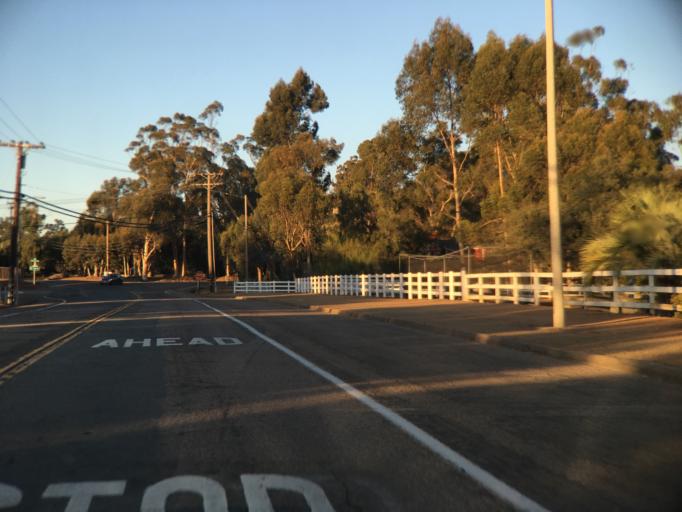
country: US
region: California
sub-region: San Diego County
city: Alpine
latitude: 32.8141
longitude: -116.7769
